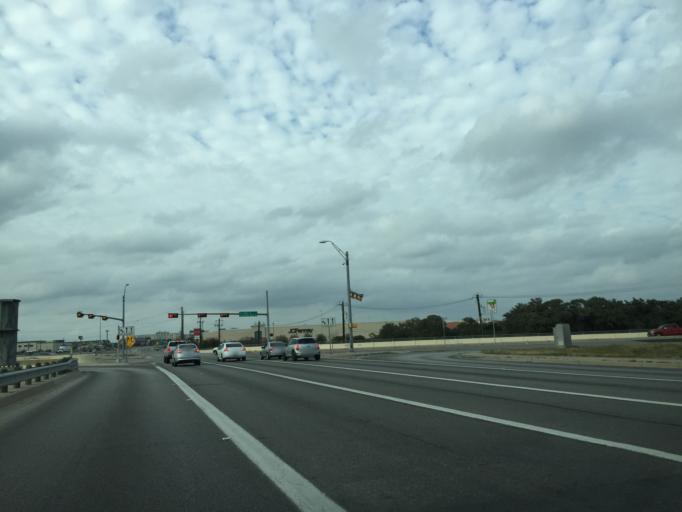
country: US
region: Texas
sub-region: Travis County
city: Wells Branch
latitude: 30.3986
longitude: -97.6727
